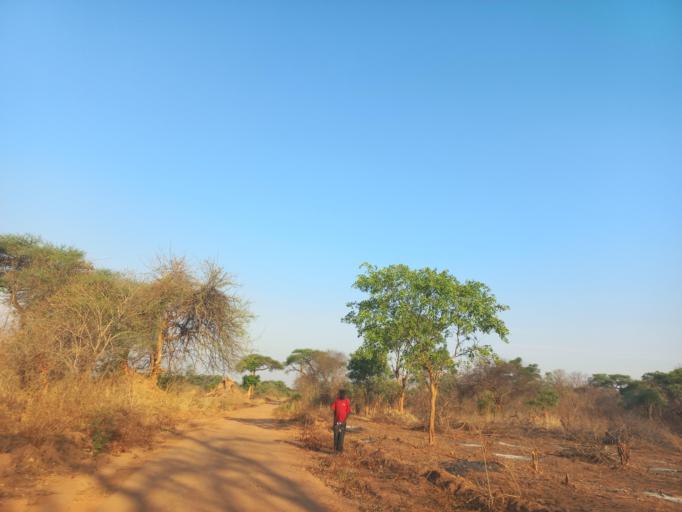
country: ZM
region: Lusaka
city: Luangwa
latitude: -15.4212
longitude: 30.2817
